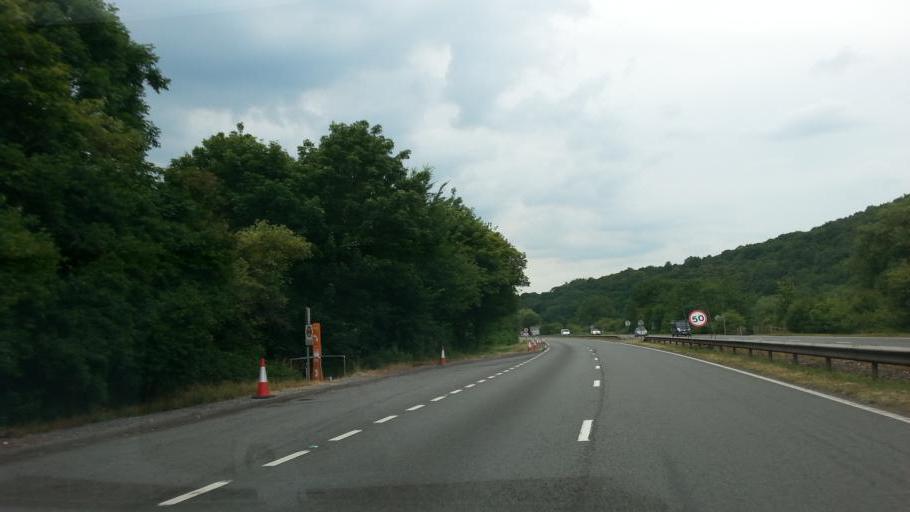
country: GB
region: Wales
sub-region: Monmouthshire
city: Monmouth
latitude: 51.8208
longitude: -2.6948
